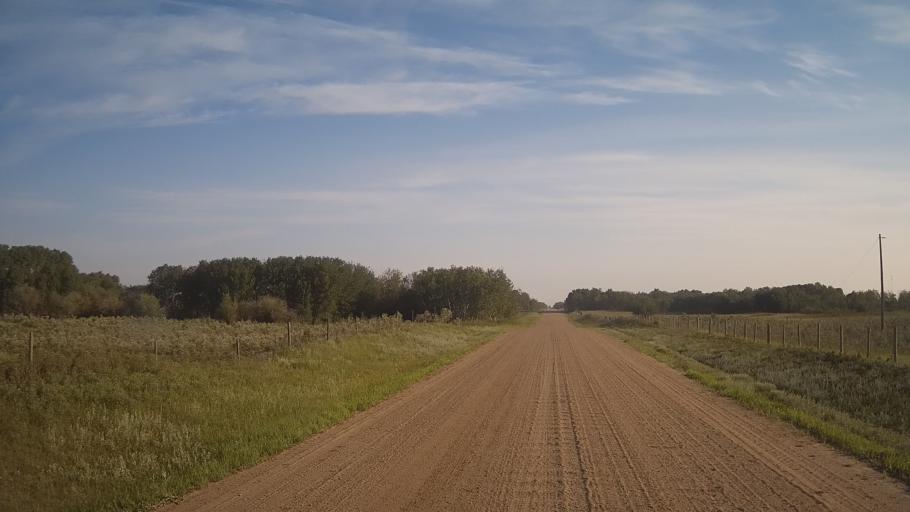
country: CA
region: Saskatchewan
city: Saskatoon
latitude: 51.8277
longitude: -106.5239
